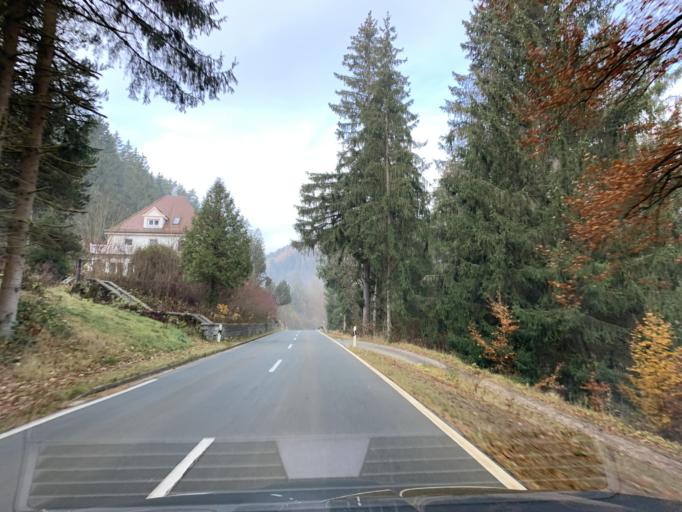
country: DE
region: Bavaria
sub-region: Upper Palatinate
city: Neunburg vorm Wald
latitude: 49.3717
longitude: 12.4228
